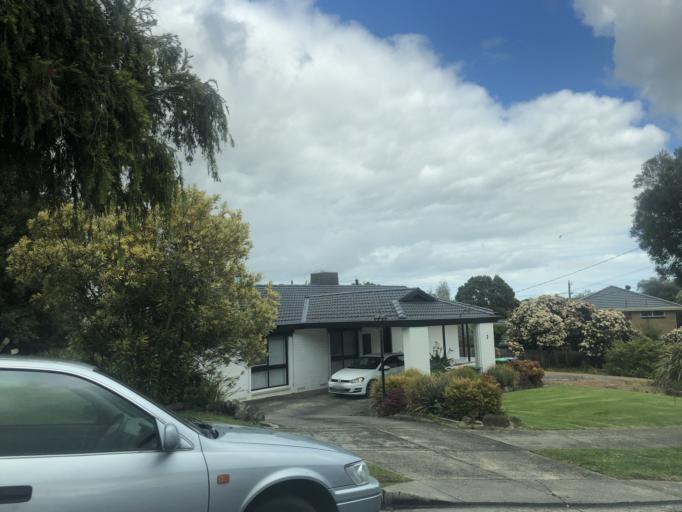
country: AU
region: Victoria
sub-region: Casey
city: Endeavour Hills
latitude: -37.9697
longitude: 145.2392
